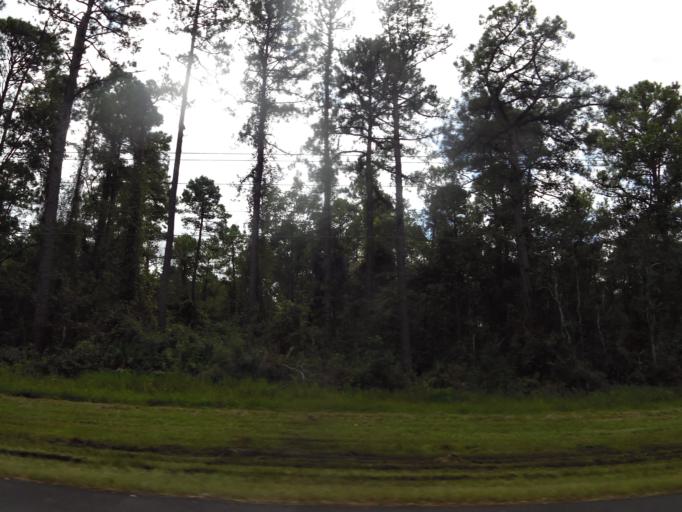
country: US
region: Florida
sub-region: Clay County
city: Middleburg
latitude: 30.1106
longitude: -81.9670
